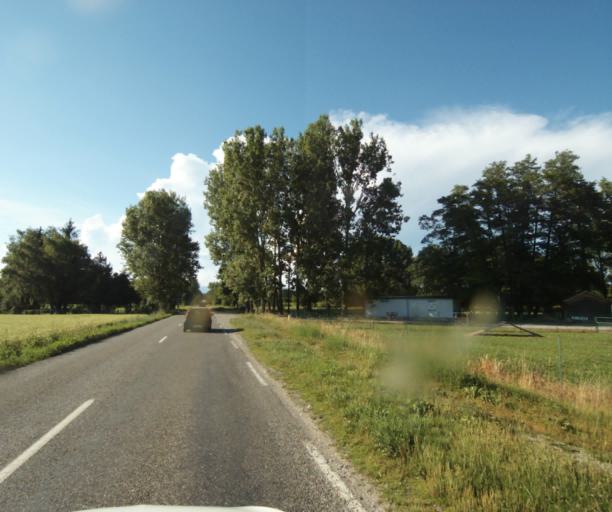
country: FR
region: Rhone-Alpes
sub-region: Departement de la Haute-Savoie
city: Douvaine
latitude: 46.3136
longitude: 6.2997
